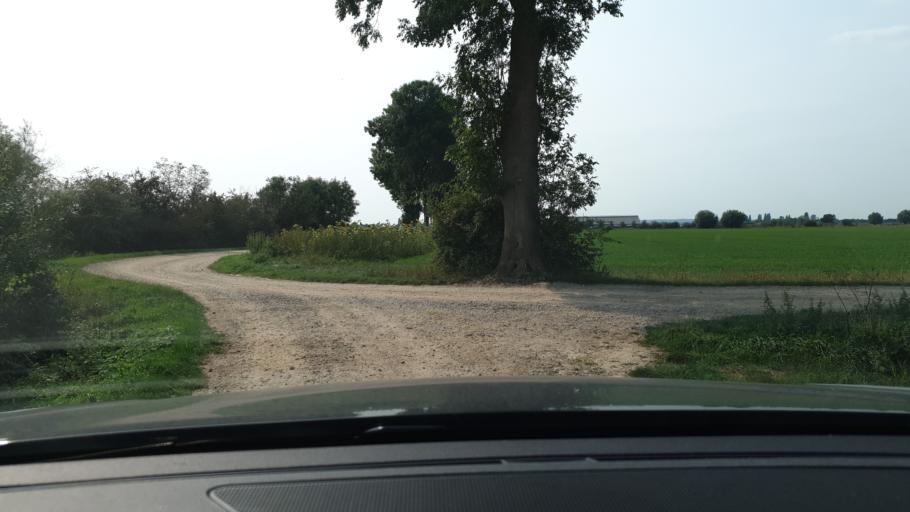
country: NL
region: Gelderland
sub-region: Gemeente Zevenaar
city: Zevenaar
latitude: 51.8526
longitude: 6.0554
